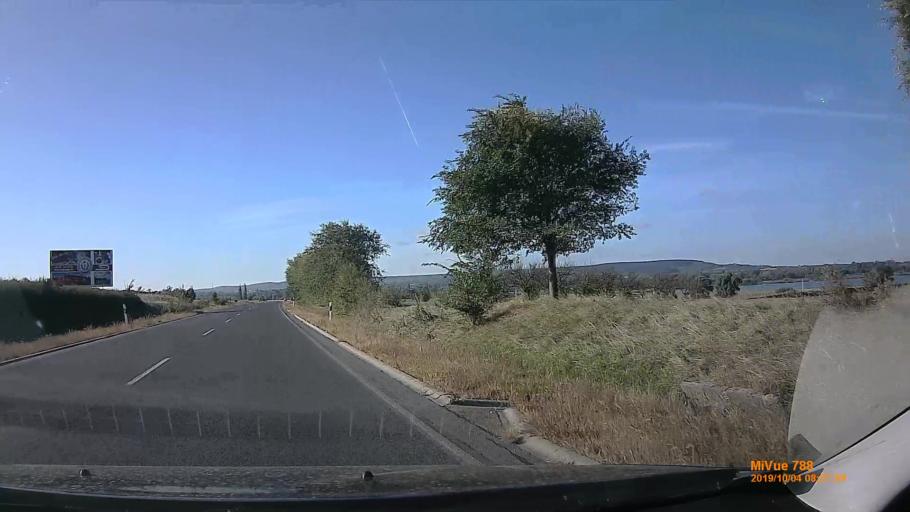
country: HU
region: Somogy
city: Balatonlelle
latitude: 46.7788
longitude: 17.7585
